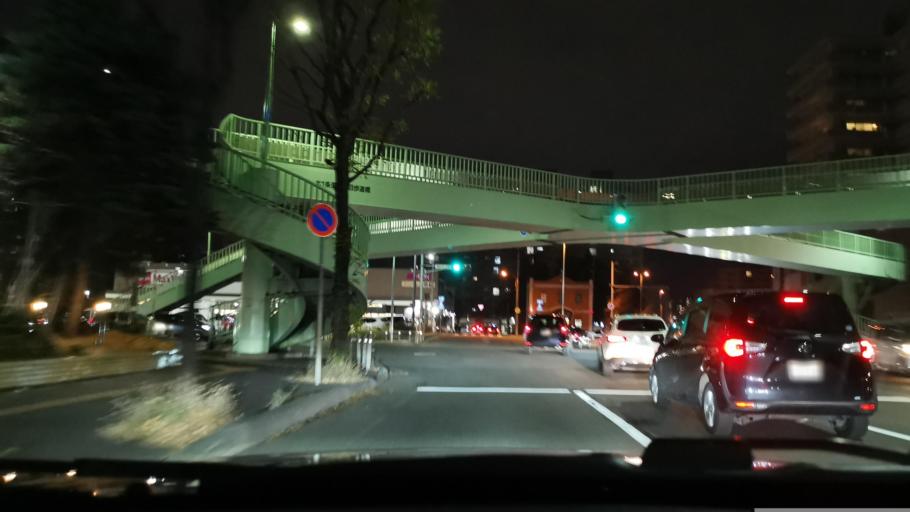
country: JP
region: Hokkaido
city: Sapporo
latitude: 43.0637
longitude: 141.3663
